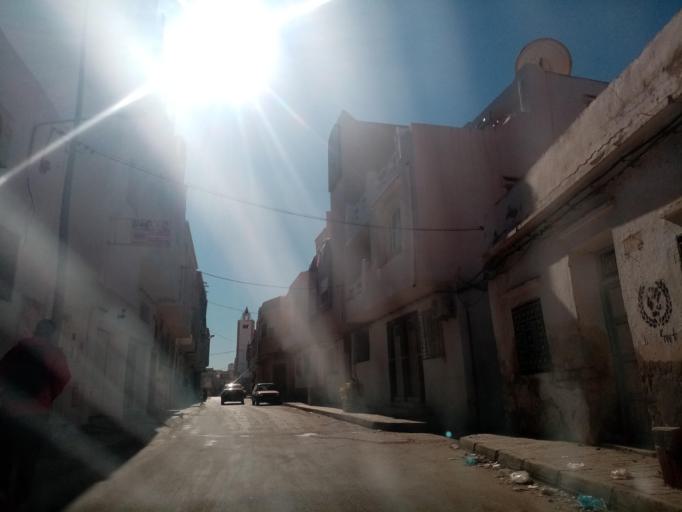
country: TN
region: Qabis
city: Gabes
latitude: 33.8809
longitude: 10.0893
